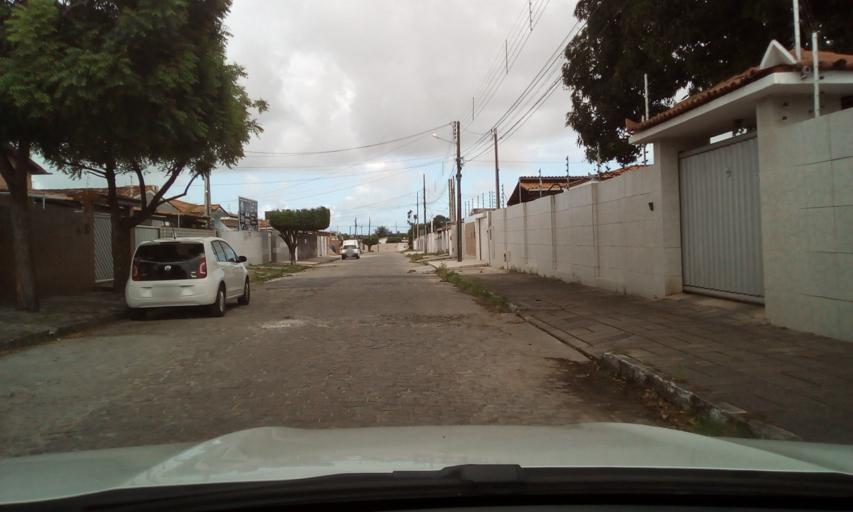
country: BR
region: Paraiba
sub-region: Joao Pessoa
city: Joao Pessoa
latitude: -7.1600
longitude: -34.8688
